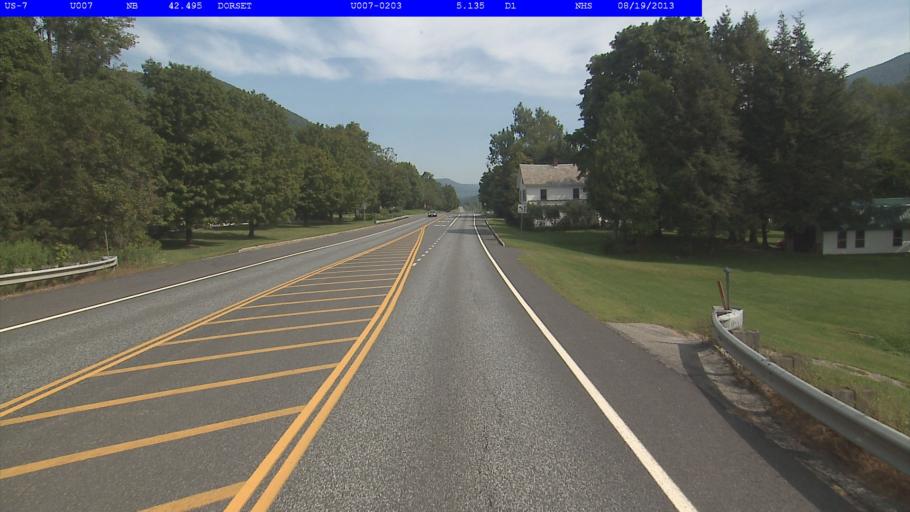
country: US
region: Vermont
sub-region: Bennington County
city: Manchester Center
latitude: 43.2827
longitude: -73.0026
